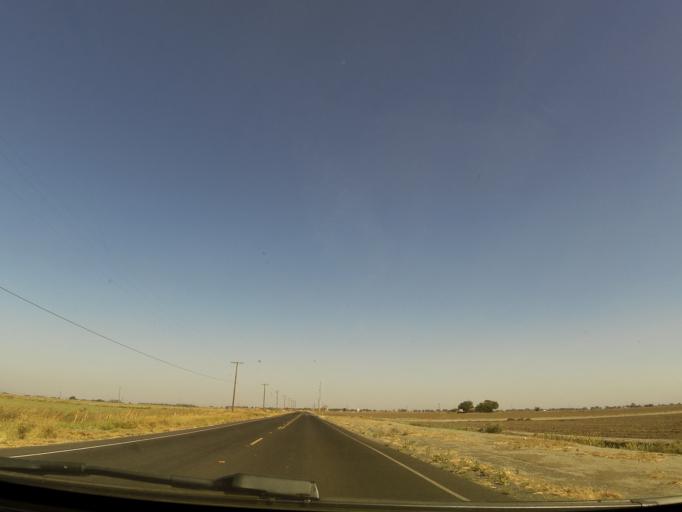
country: US
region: California
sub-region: San Joaquin County
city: Tracy
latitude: 37.8510
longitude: -121.4155
